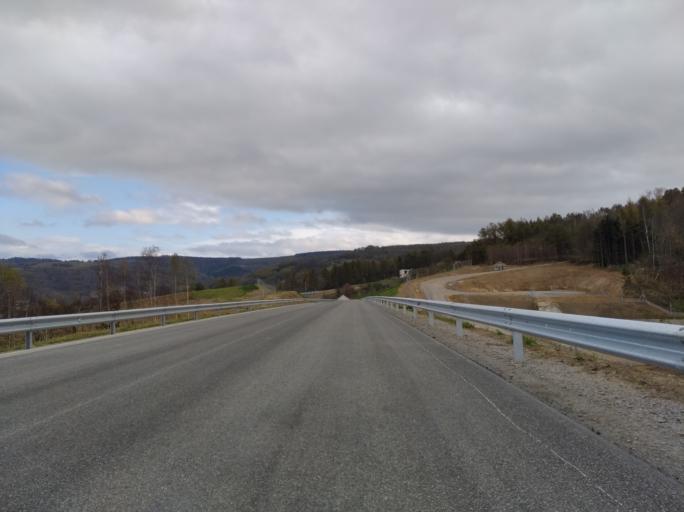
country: PL
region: Subcarpathian Voivodeship
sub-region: Powiat strzyzowski
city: Strzyzow
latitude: 49.8620
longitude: 21.8065
